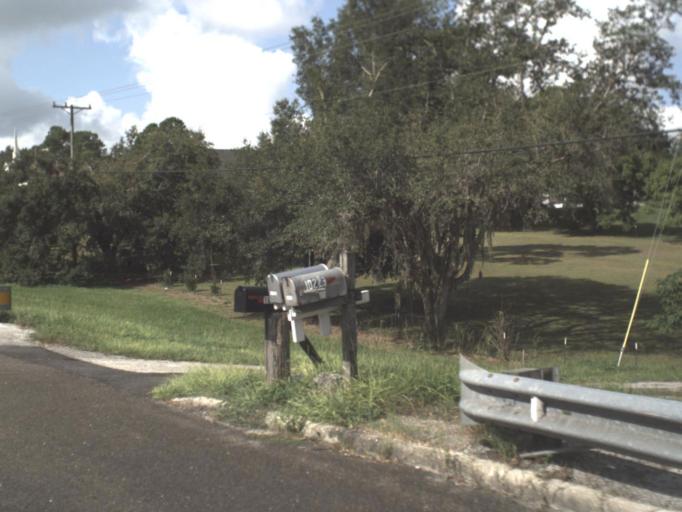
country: US
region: Florida
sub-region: Pasco County
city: Zephyrhills North
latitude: 28.3047
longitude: -82.1878
